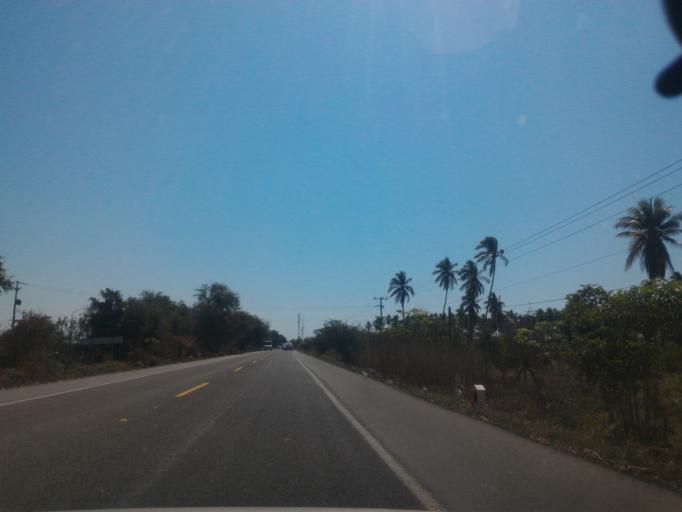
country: MX
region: Colima
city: Tecoman
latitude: 18.8371
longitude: -103.8202
